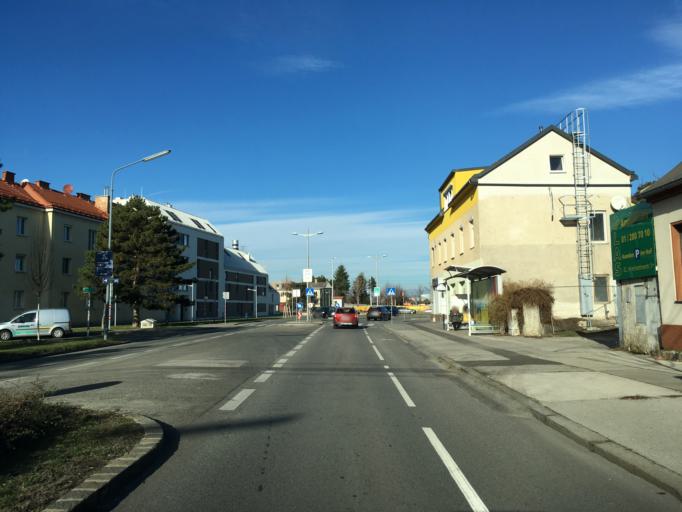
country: AT
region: Lower Austria
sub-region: Politischer Bezirk Wien-Umgebung
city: Gerasdorf bei Wien
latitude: 48.2471
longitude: 16.4517
